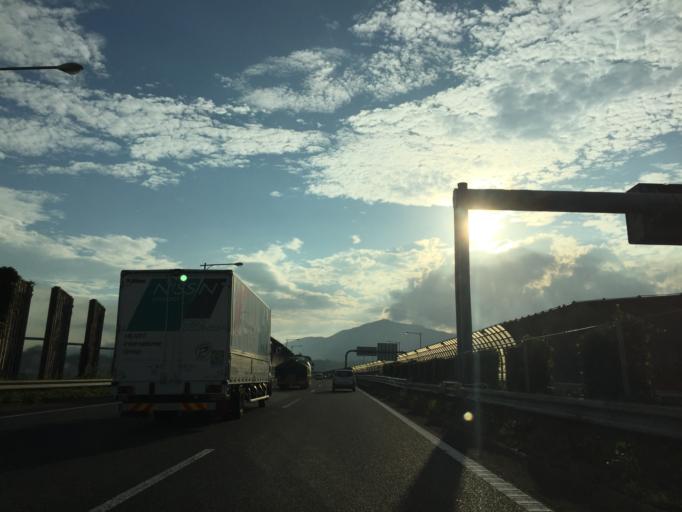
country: JP
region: Kanagawa
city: Atsugi
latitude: 35.4249
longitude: 139.3543
